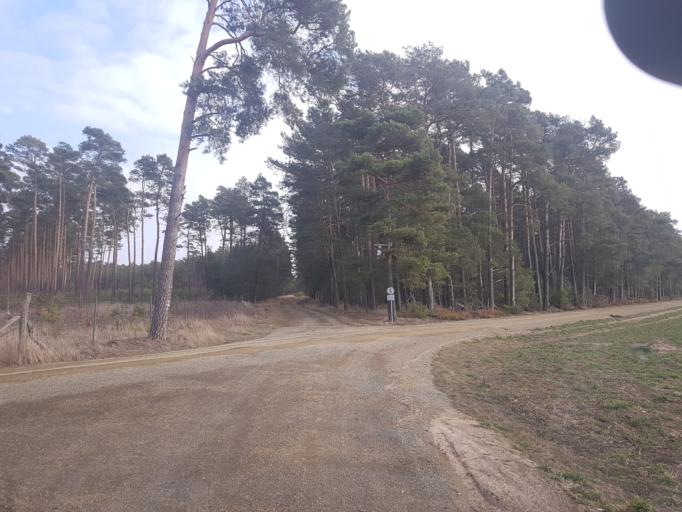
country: DE
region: Brandenburg
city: Hohenbucko
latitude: 51.7718
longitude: 13.4847
